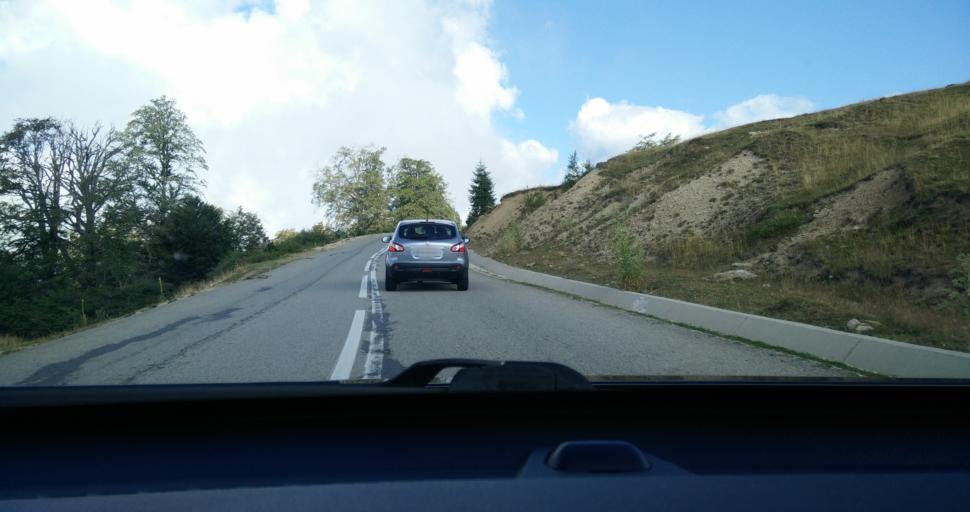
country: RO
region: Gorj
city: Novaci-Straini
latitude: 45.2315
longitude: 23.6870
